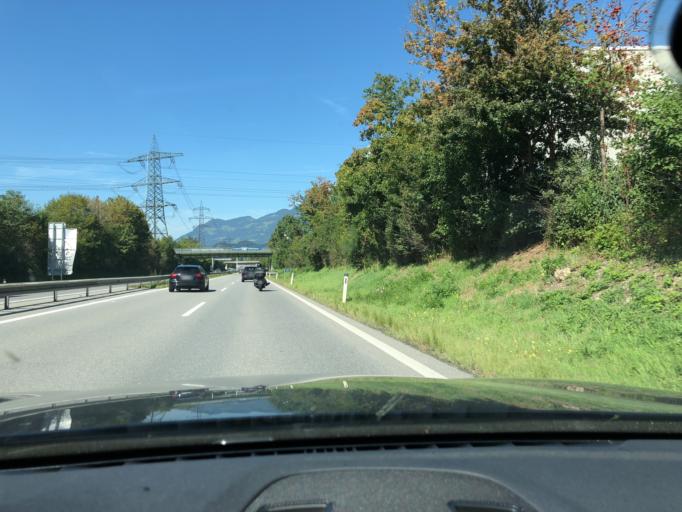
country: AT
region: Vorarlberg
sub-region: Politischer Bezirk Bludenz
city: Bludenz
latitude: 47.1455
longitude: 9.8202
